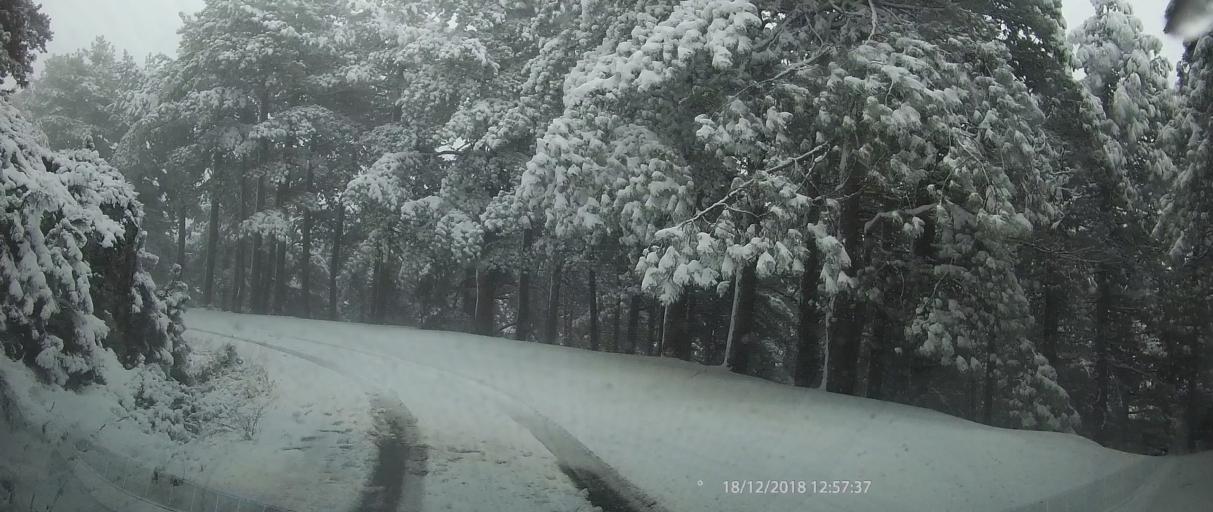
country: GR
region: Central Macedonia
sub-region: Nomos Pierias
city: Litochoro
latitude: 40.1070
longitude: 22.4652
